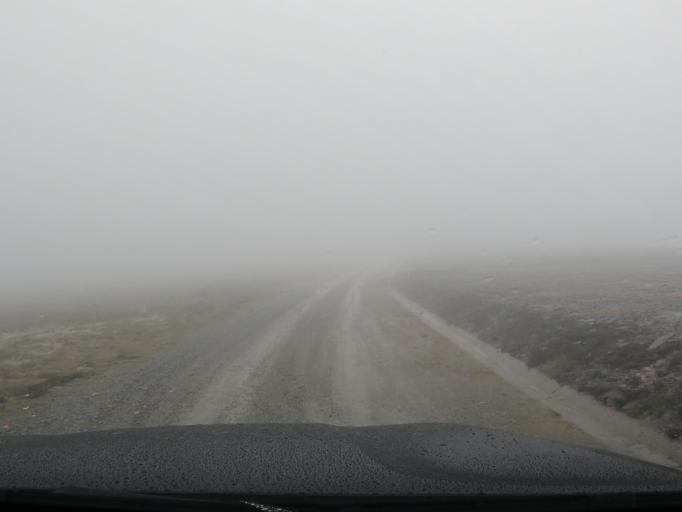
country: PT
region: Vila Real
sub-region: Vila Real
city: Vila Real
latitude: 41.3304
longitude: -7.8373
